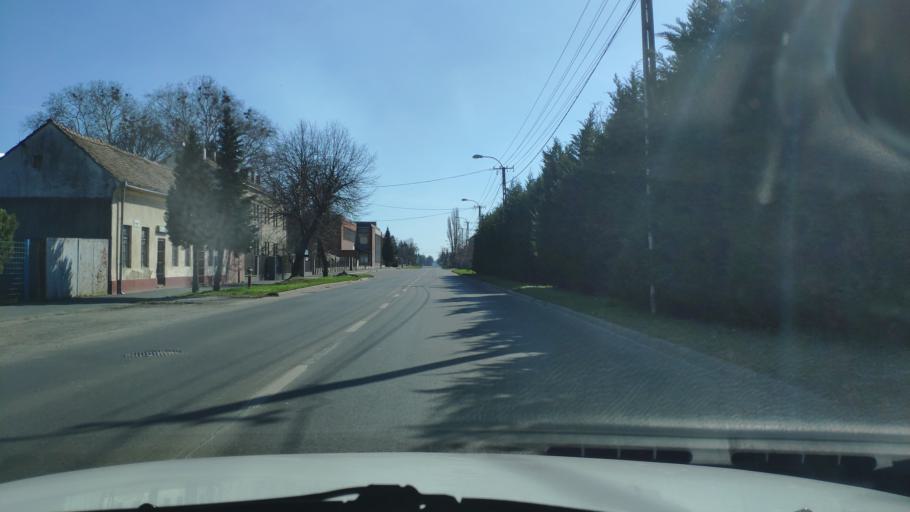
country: HU
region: Zala
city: Nagykanizsa
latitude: 46.4384
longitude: 16.9886
